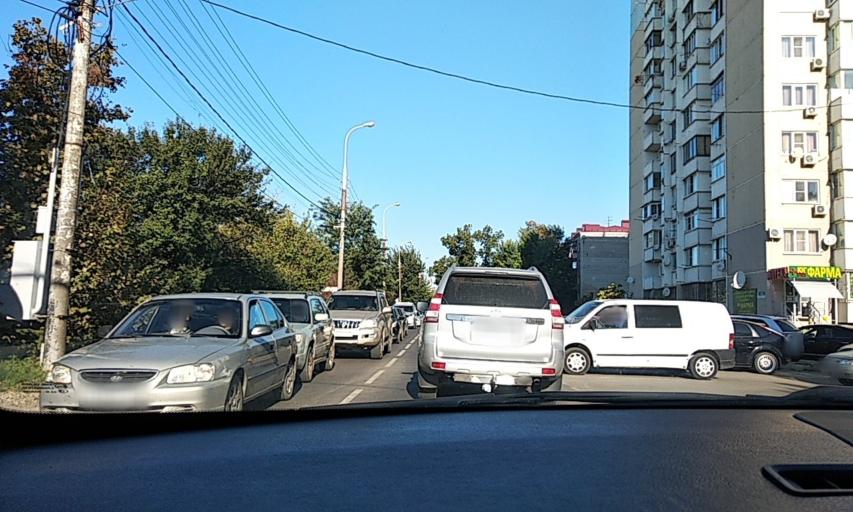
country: RU
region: Krasnodarskiy
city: Pashkovskiy
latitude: 45.0294
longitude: 39.1232
